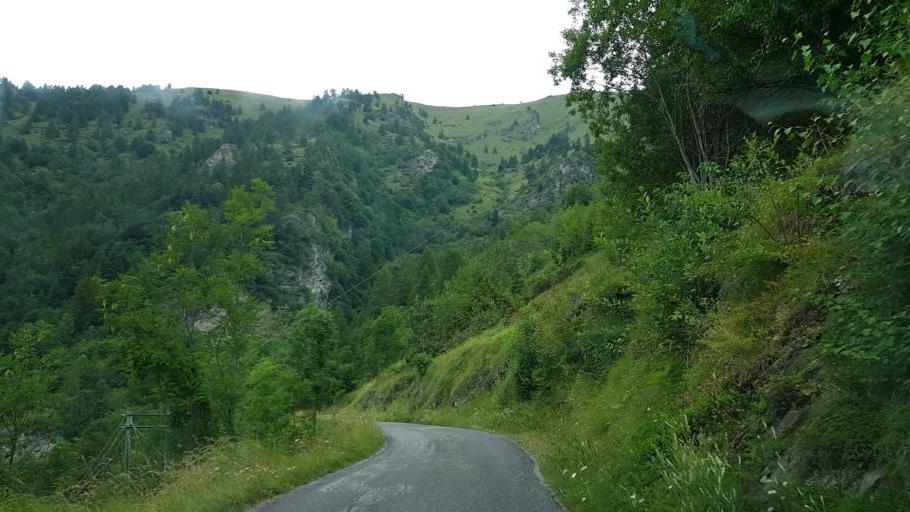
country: IT
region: Piedmont
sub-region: Provincia di Cuneo
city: Stroppo
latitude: 44.5190
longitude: 7.1189
